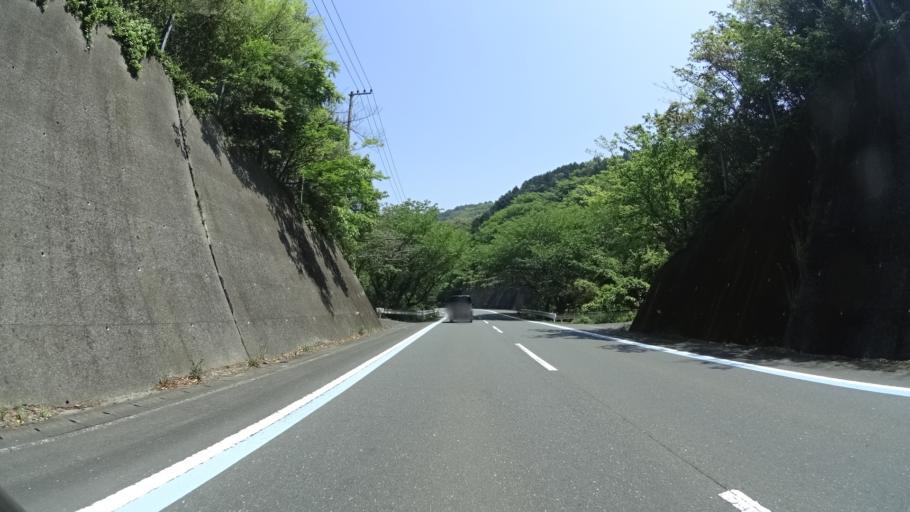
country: JP
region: Ehime
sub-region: Nishiuwa-gun
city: Ikata-cho
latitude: 33.5478
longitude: 132.4234
